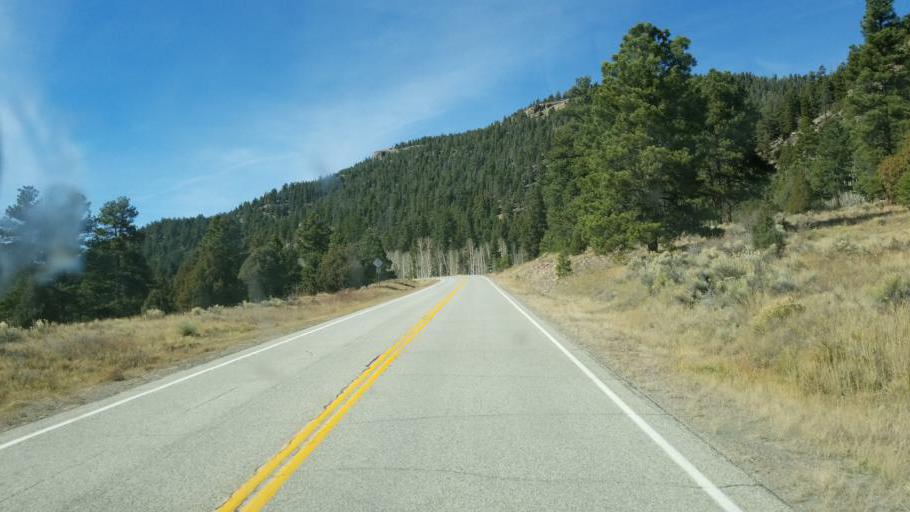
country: US
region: Colorado
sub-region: Conejos County
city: Conejos
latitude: 37.0733
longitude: -106.2646
